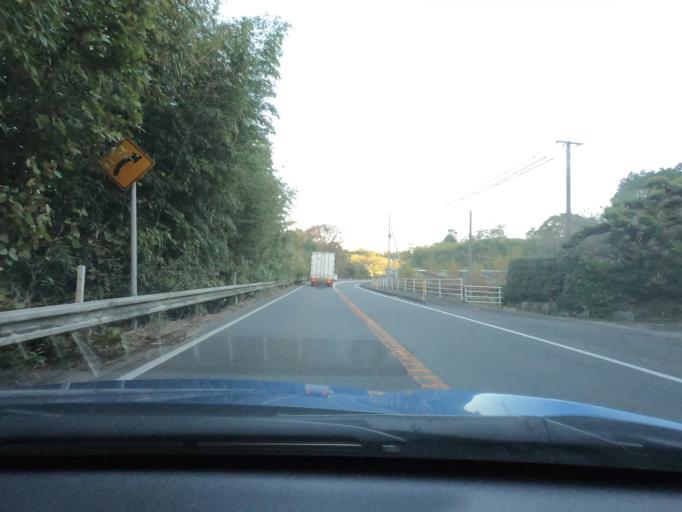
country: JP
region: Kagoshima
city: Satsumasendai
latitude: 31.8438
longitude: 130.2782
